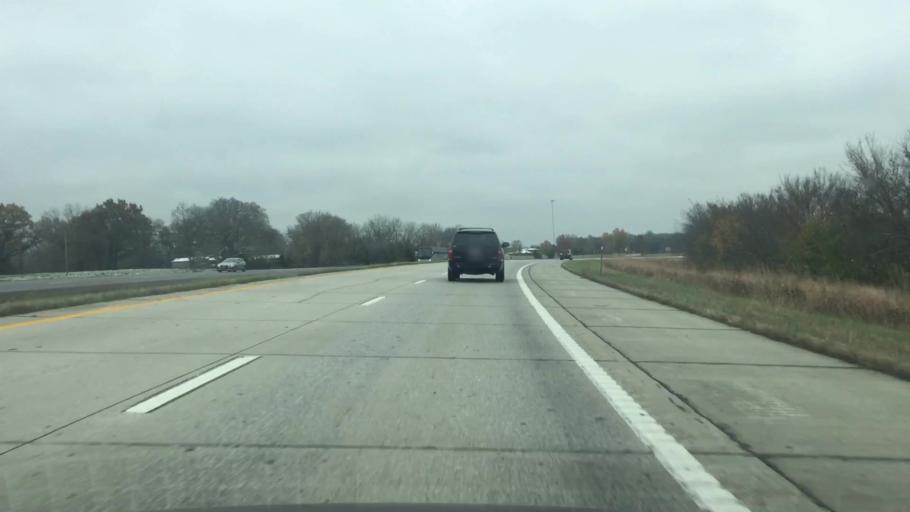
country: US
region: Missouri
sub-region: Saint Clair County
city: Osceola
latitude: 38.0124
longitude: -93.6594
